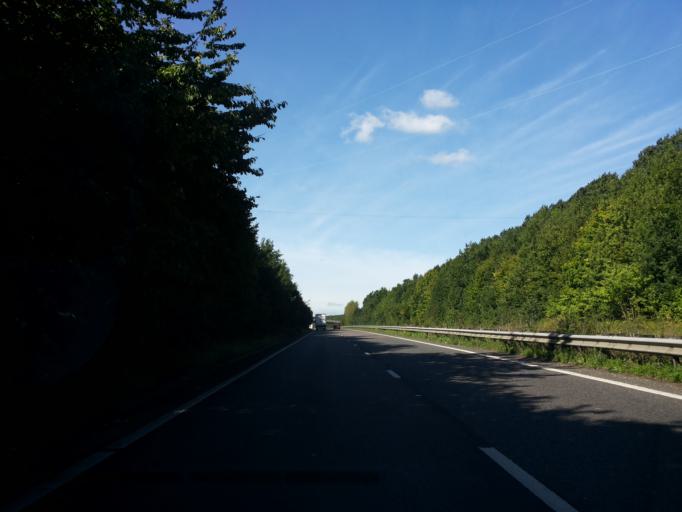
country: GB
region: England
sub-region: Kent
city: Blean
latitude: 51.2777
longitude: 1.0455
